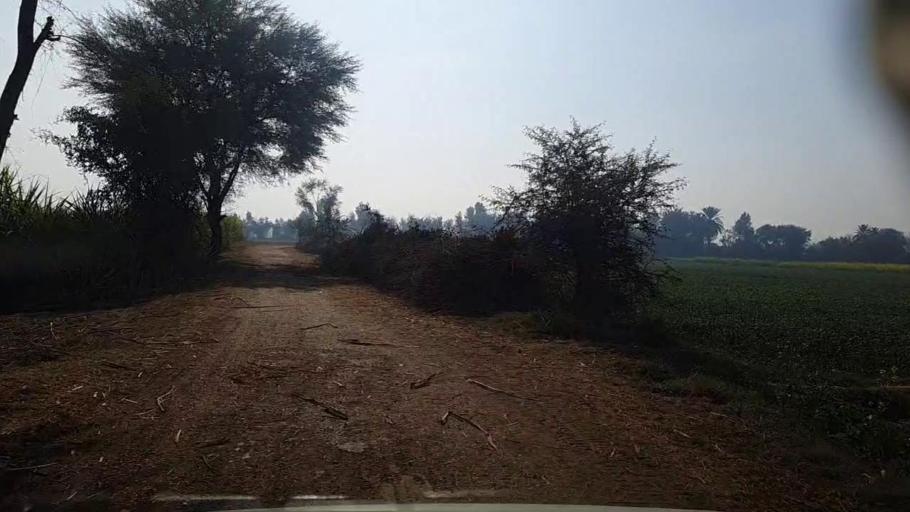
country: PK
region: Sindh
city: Khairpur
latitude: 27.9430
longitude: 69.6593
